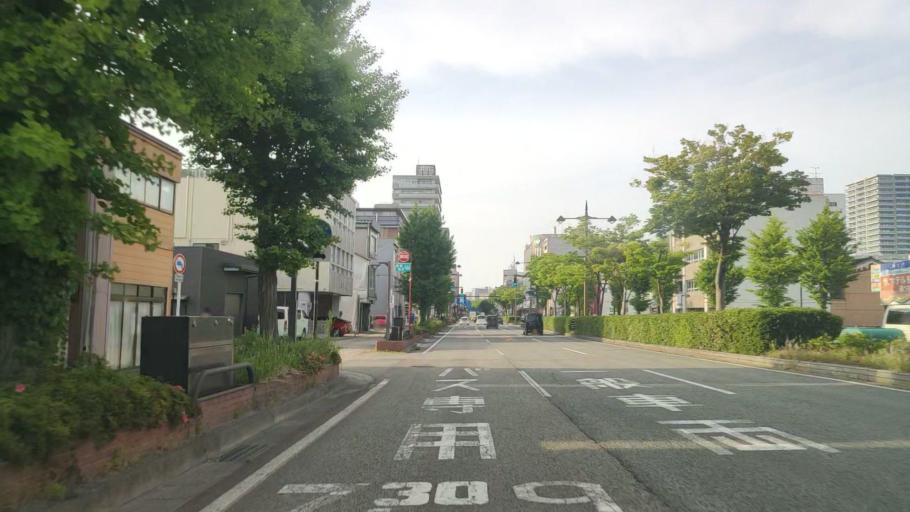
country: JP
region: Toyama
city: Toyama-shi
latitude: 36.6863
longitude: 137.2120
